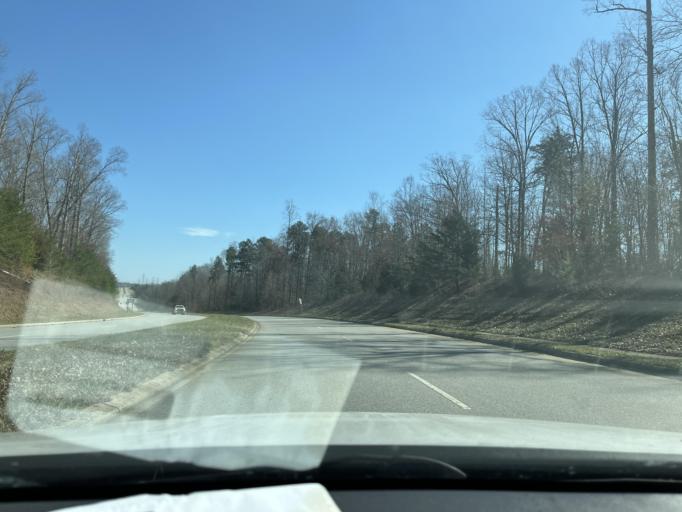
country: US
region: North Carolina
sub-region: Guilford County
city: Jamestown
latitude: 36.0115
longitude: -79.9270
